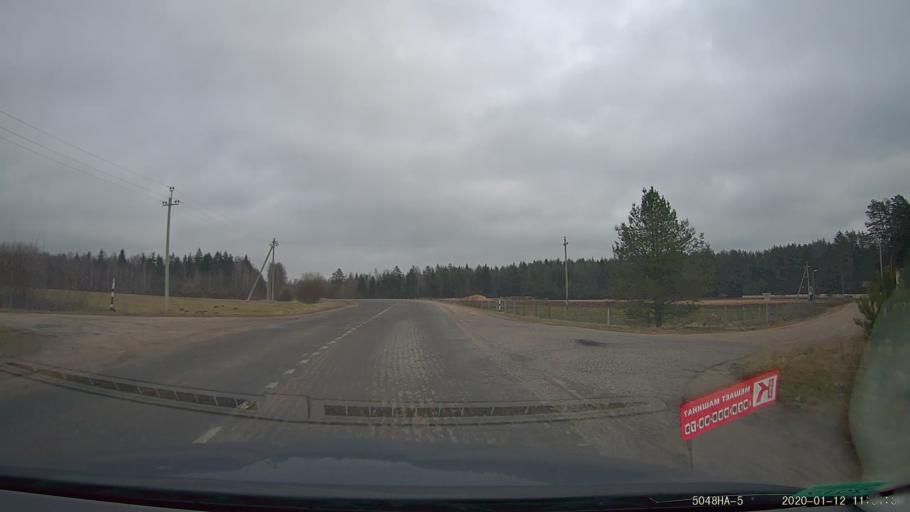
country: BY
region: Minsk
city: Rakaw
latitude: 53.9615
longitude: 27.1196
